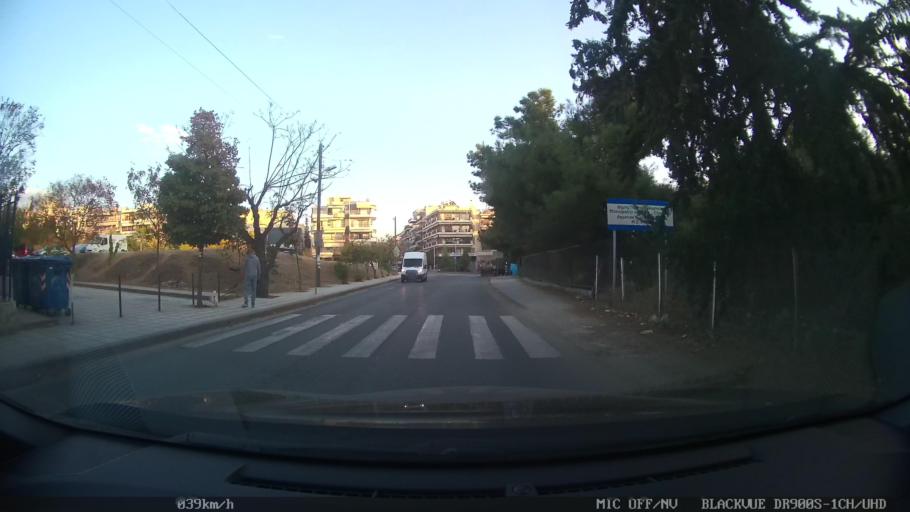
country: GR
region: Central Macedonia
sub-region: Nomos Thessalonikis
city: Triandria
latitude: 40.6089
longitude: 22.9822
